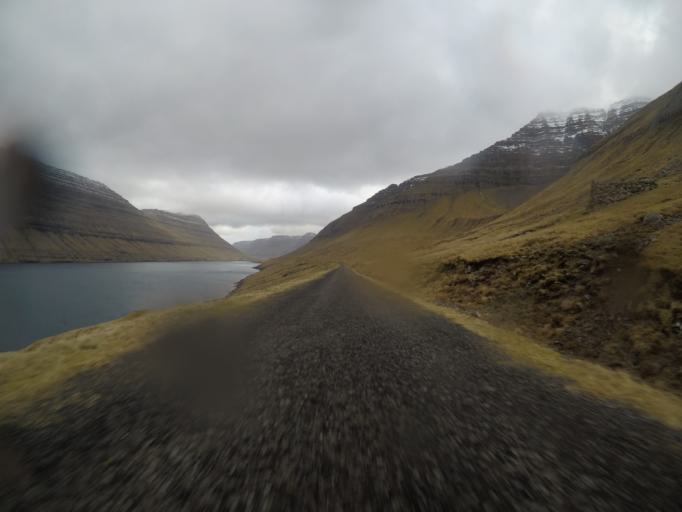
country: FO
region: Nordoyar
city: Klaksvik
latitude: 62.3221
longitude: -6.5604
